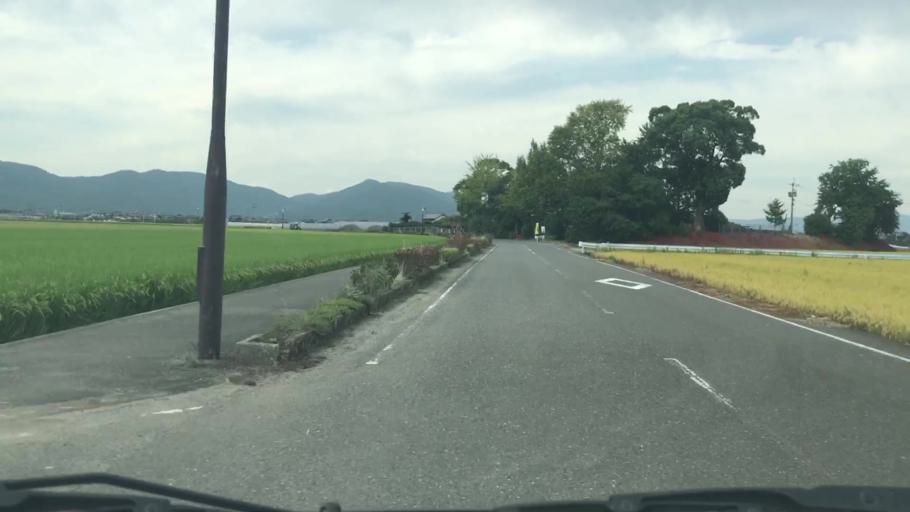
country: JP
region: Saga Prefecture
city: Kashima
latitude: 33.1449
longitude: 130.1443
